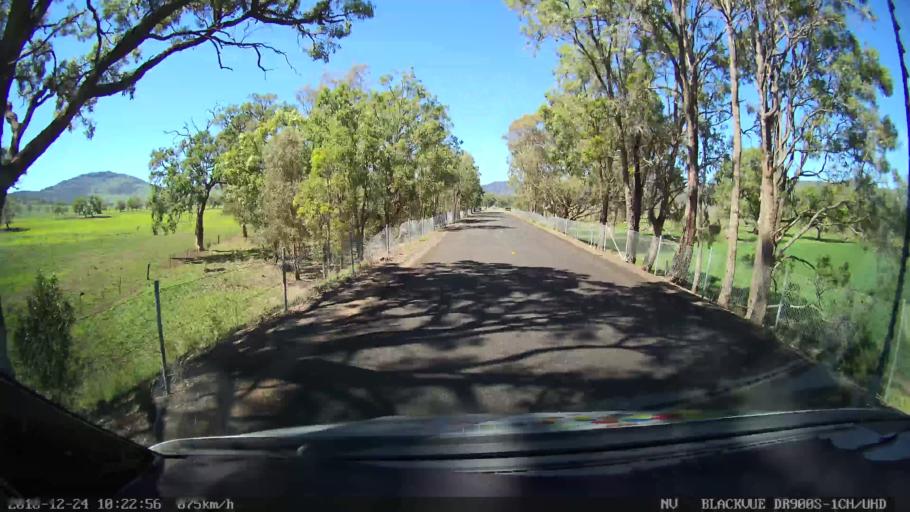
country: AU
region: New South Wales
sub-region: Liverpool Plains
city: Quirindi
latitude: -31.7698
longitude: 150.5415
